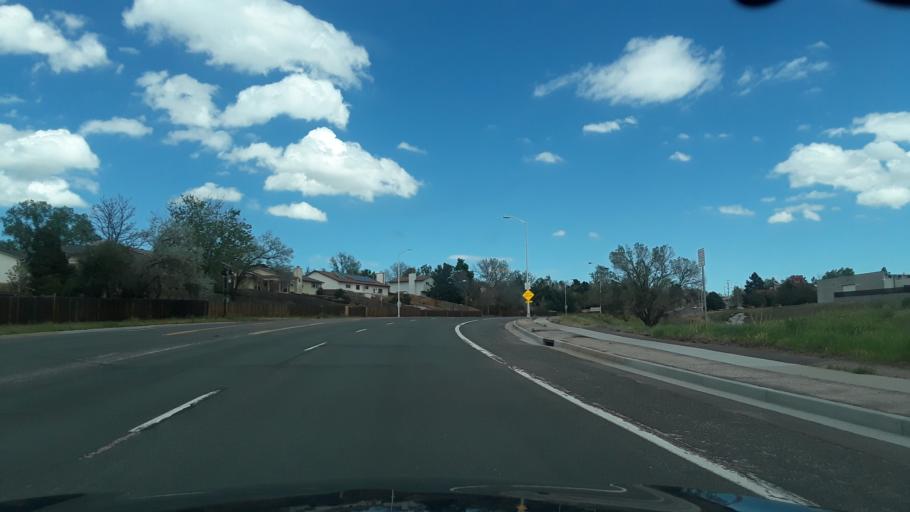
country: US
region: Colorado
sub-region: El Paso County
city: Air Force Academy
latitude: 38.9442
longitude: -104.7840
